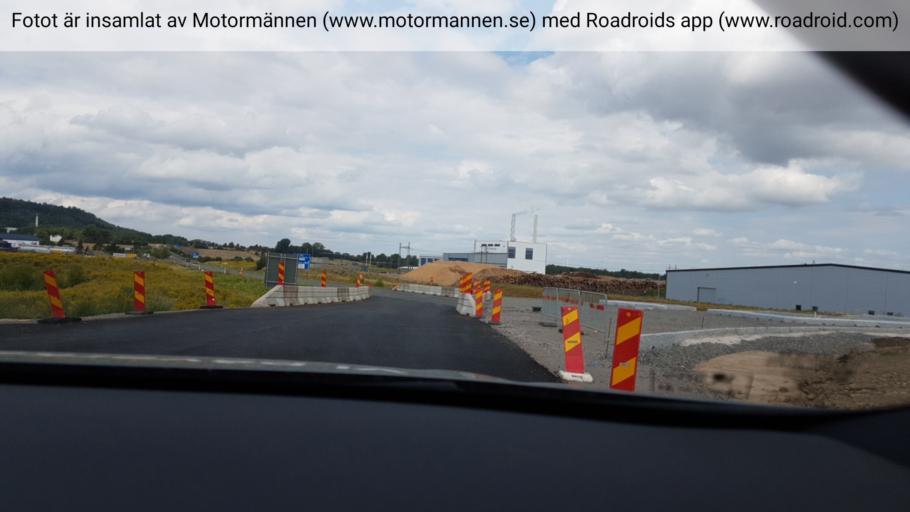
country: SE
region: Vaestra Goetaland
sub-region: Falkopings Kommun
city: Falkoeping
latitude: 58.1815
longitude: 13.5754
